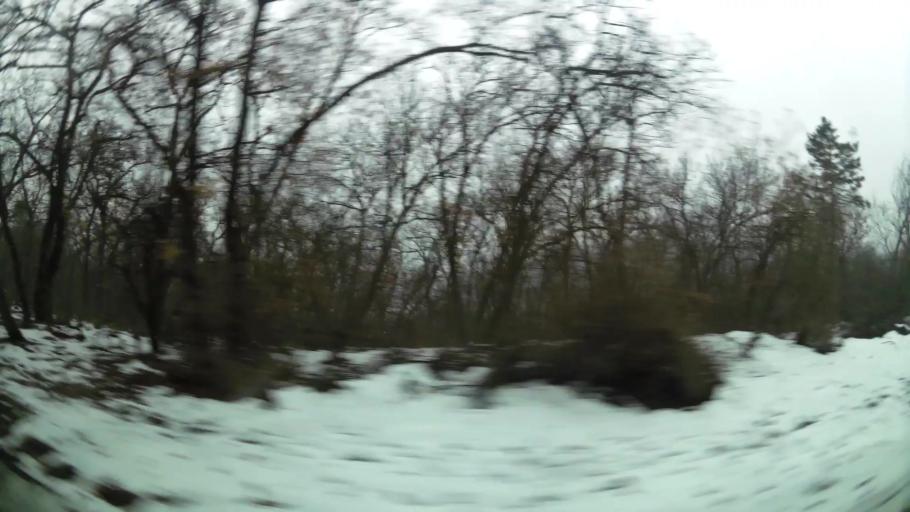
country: RS
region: Central Serbia
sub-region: Belgrade
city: Cukarica
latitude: 44.7771
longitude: 20.4329
